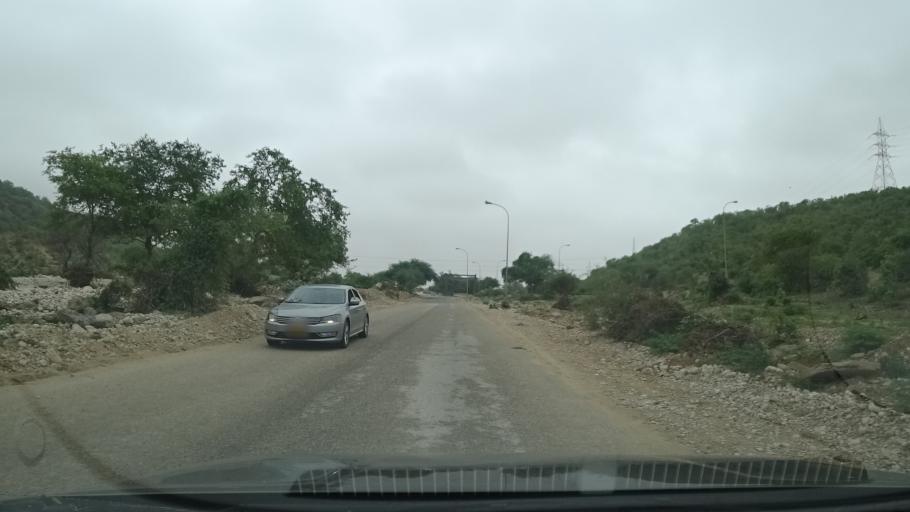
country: OM
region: Zufar
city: Salalah
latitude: 17.1023
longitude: 54.0764
